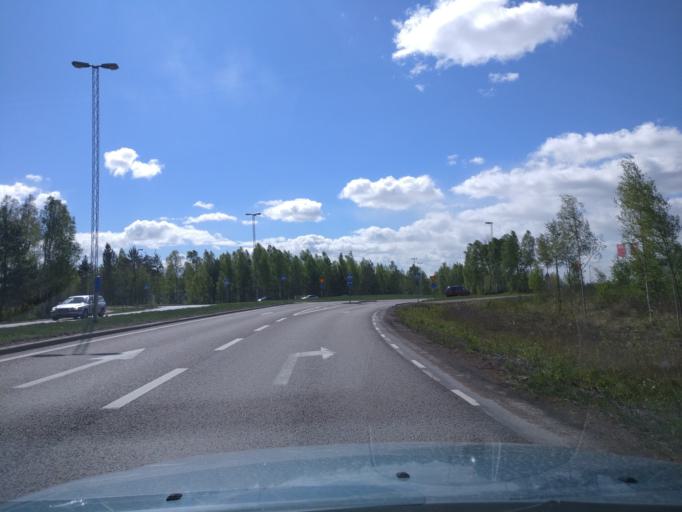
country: SE
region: Vaermland
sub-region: Karlstads Kommun
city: Skattkarr
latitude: 59.3960
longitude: 13.5824
